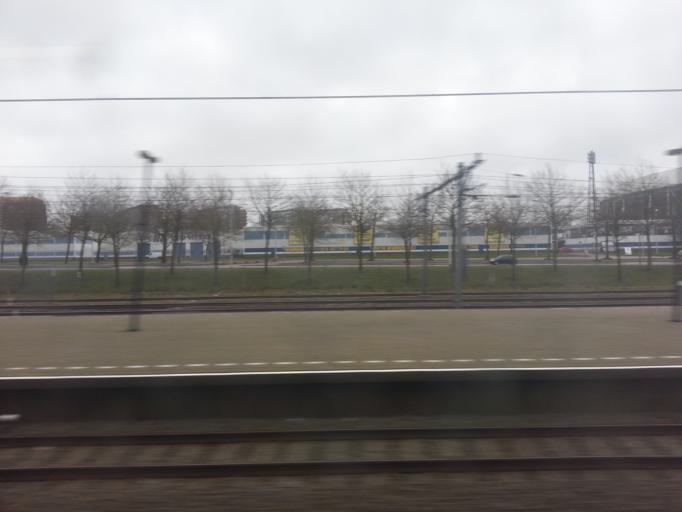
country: NL
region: South Holland
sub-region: Gemeente Barendrecht
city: Barendrecht
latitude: 51.8941
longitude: 4.5188
